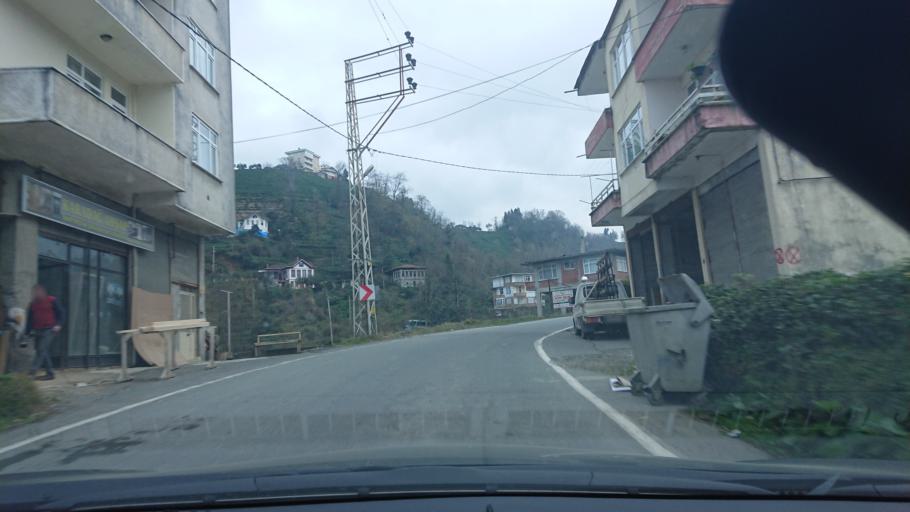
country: TR
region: Rize
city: Rize
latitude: 41.0247
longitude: 40.5035
